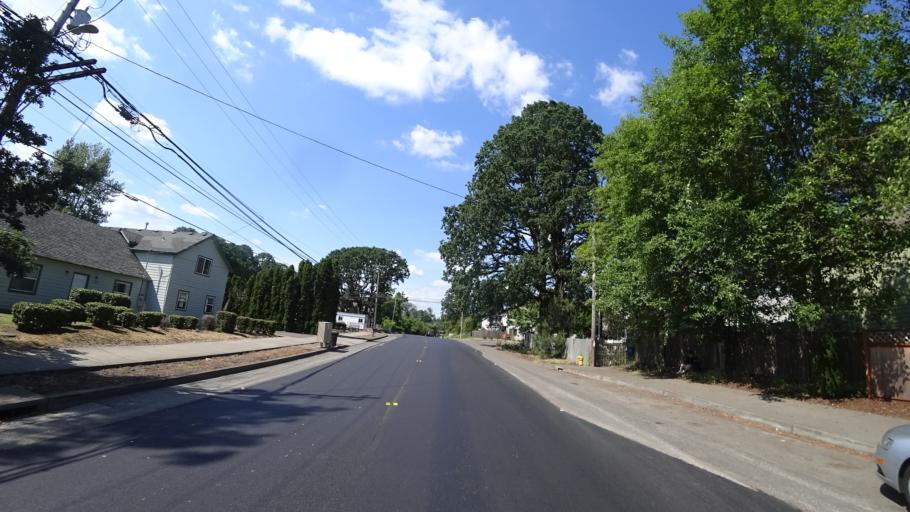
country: US
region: Oregon
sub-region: Washington County
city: Metzger
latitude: 45.4415
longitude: -122.7654
